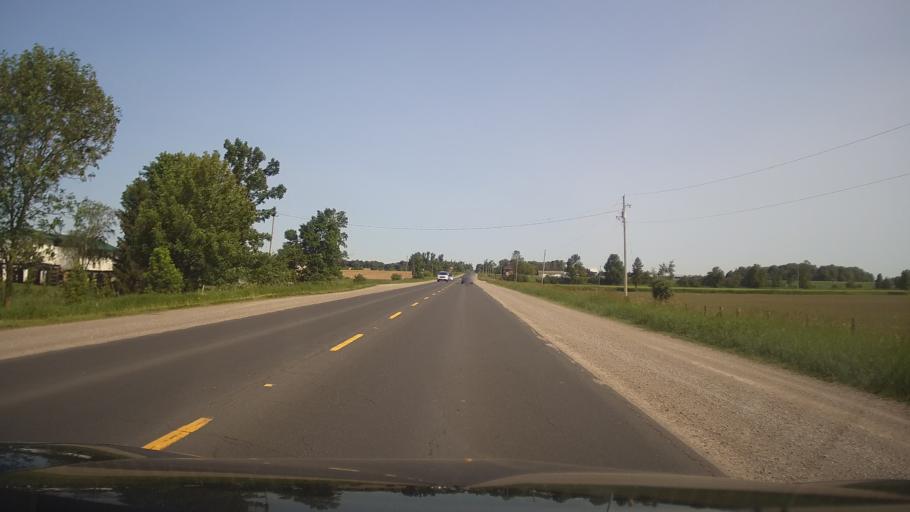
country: CA
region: Ontario
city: Omemee
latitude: 44.3229
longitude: -78.6839
